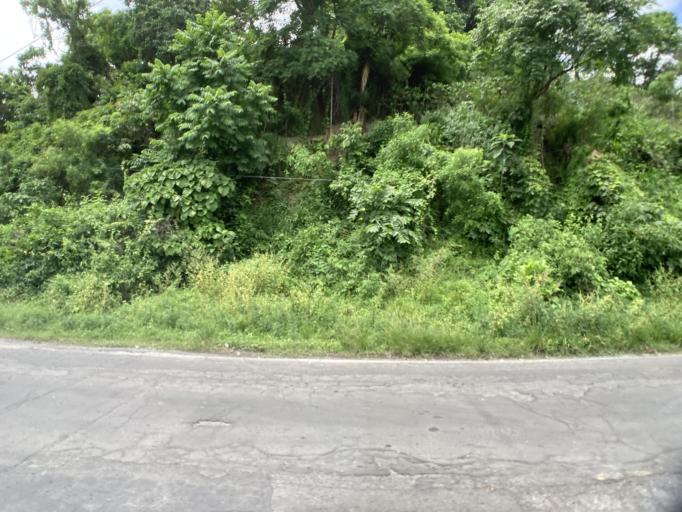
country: GT
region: Guatemala
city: Amatitlan
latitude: 14.4614
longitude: -90.5839
